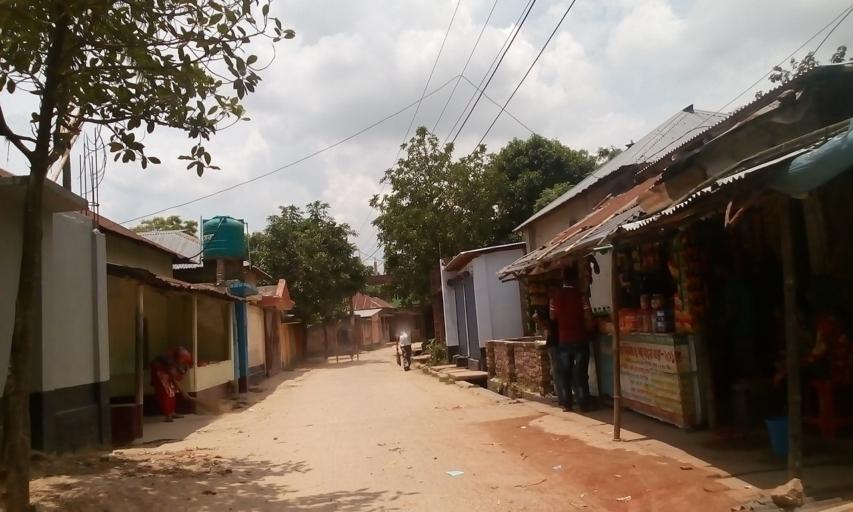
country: IN
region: West Bengal
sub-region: Dakshin Dinajpur
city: Balurghat
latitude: 25.3901
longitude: 88.9875
